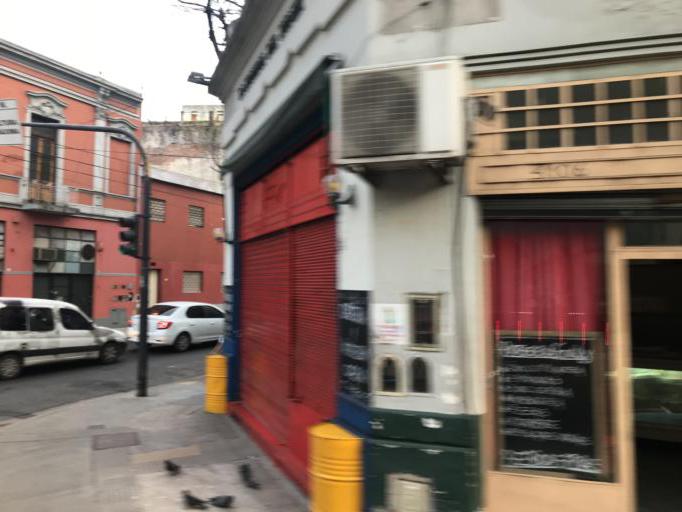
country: AR
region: Buenos Aires F.D.
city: Buenos Aires
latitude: -34.6068
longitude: -58.4101
